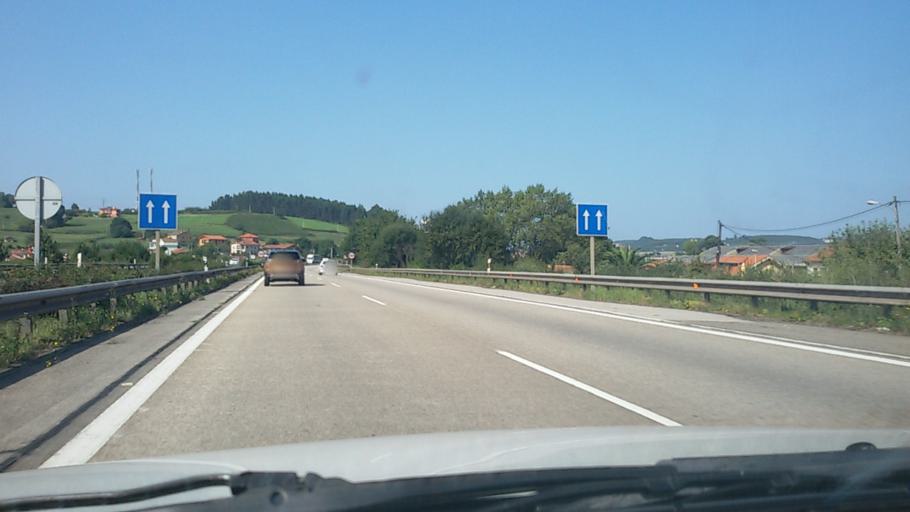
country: ES
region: Asturias
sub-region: Province of Asturias
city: Corvera de Asturias
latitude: 43.5505
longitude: -5.8750
